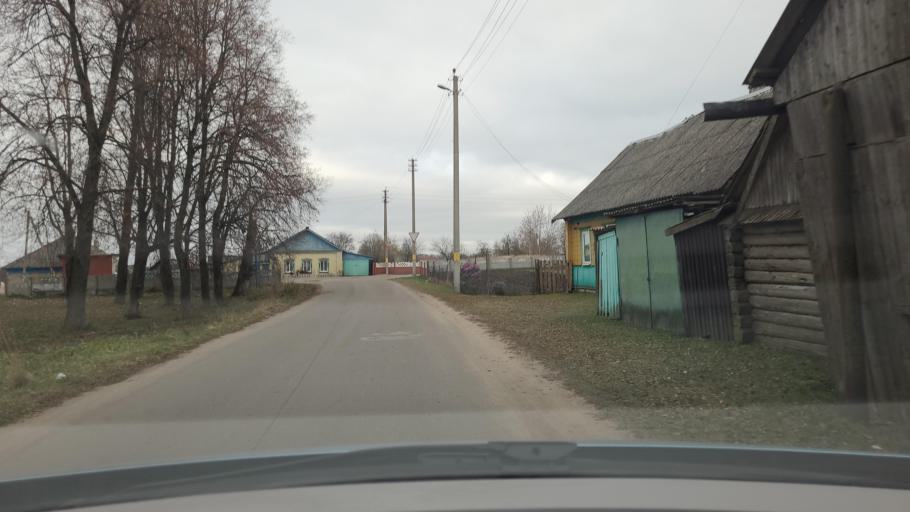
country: BY
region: Minsk
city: Khalopyenichy
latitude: 54.5133
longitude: 28.9594
